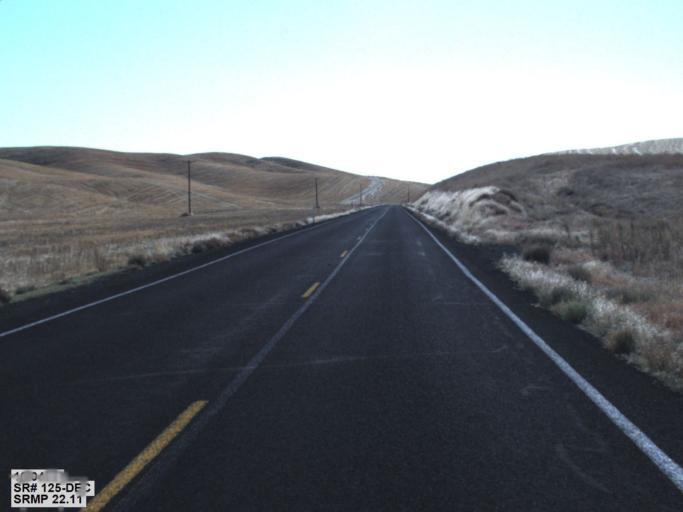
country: US
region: Washington
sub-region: Walla Walla County
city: Waitsburg
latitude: 46.2772
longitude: -118.3462
